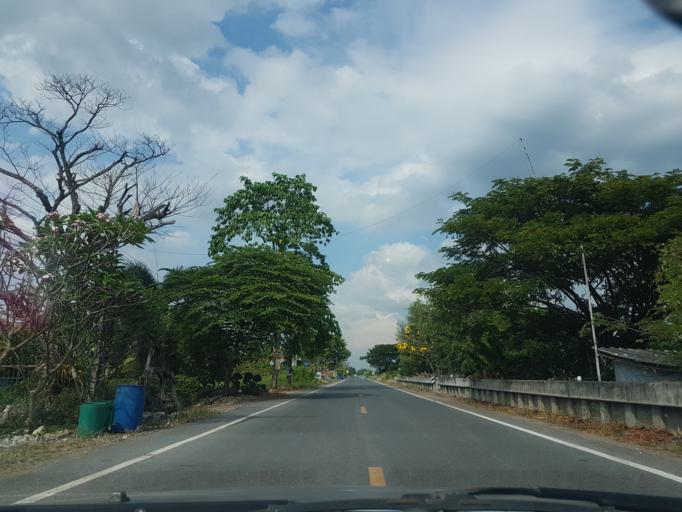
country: TH
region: Pathum Thani
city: Nong Suea
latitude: 14.1717
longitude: 100.8915
